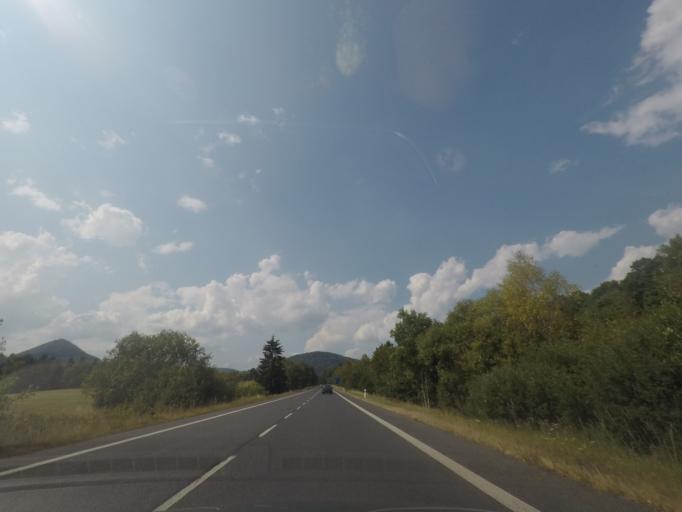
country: CZ
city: Cvikov
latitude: 50.7865
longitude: 14.6108
